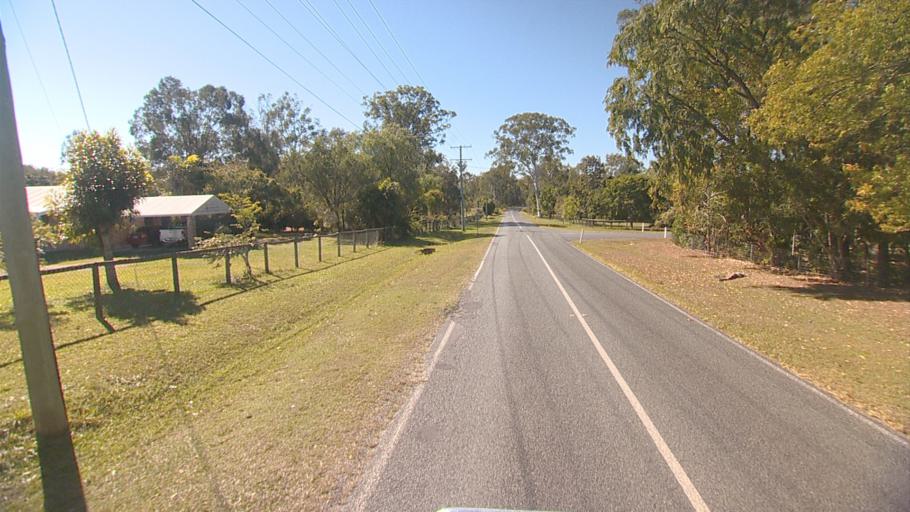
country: AU
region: Queensland
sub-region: Logan
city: Park Ridge South
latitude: -27.7236
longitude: 153.0545
